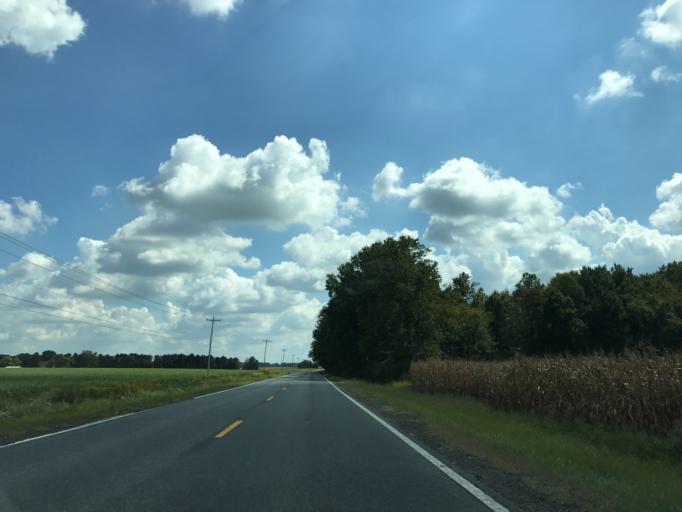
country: US
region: Maryland
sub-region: Queen Anne's County
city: Centreville
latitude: 39.0078
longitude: -75.9853
